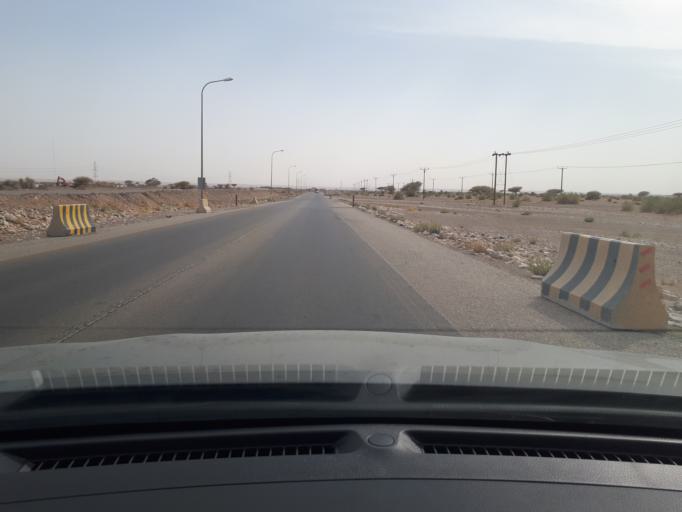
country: OM
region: Ash Sharqiyah
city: Badiyah
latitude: 22.4853
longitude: 58.9197
